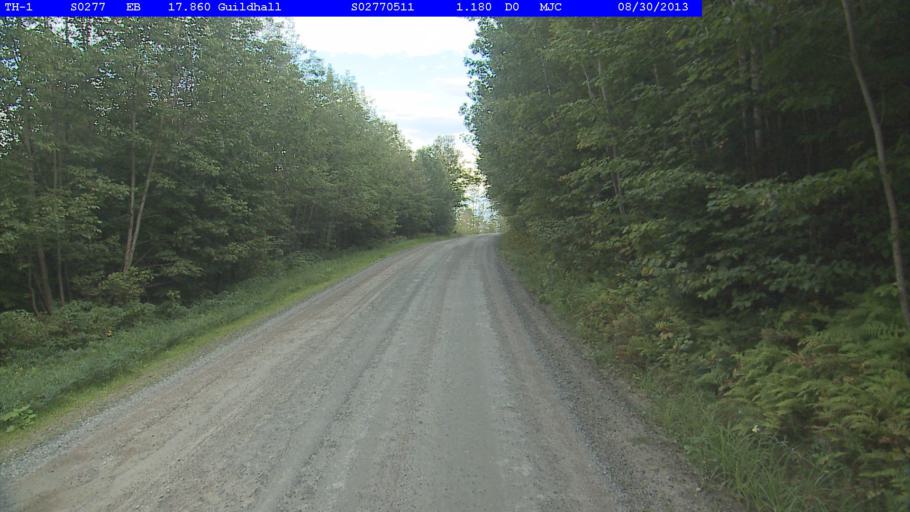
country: US
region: Vermont
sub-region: Essex County
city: Guildhall
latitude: 44.5690
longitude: -71.6475
